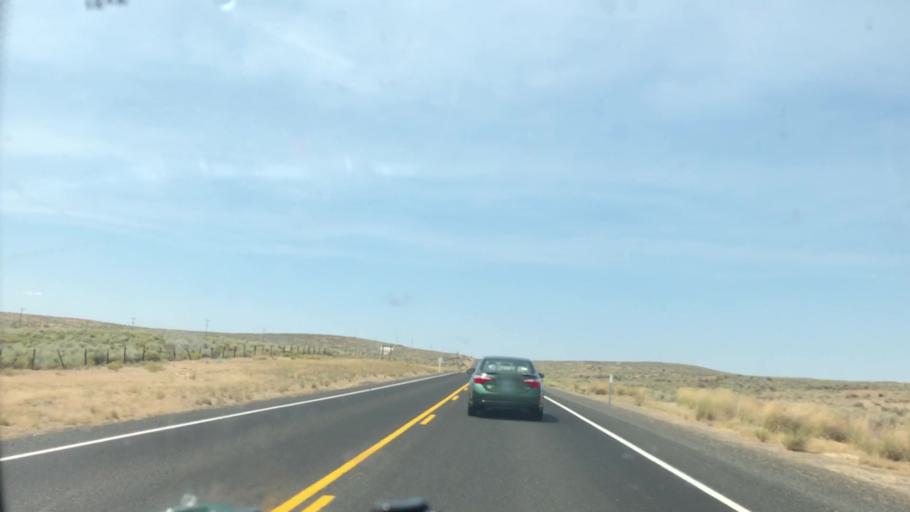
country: US
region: Idaho
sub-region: Owyhee County
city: Murphy
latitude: 42.9850
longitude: -117.0543
